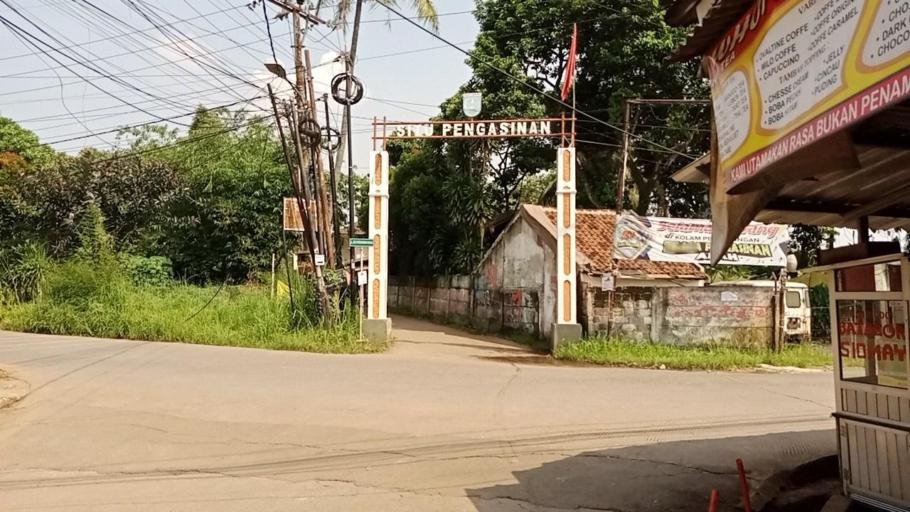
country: ID
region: West Java
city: Parung
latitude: -6.4222
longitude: 106.7524
